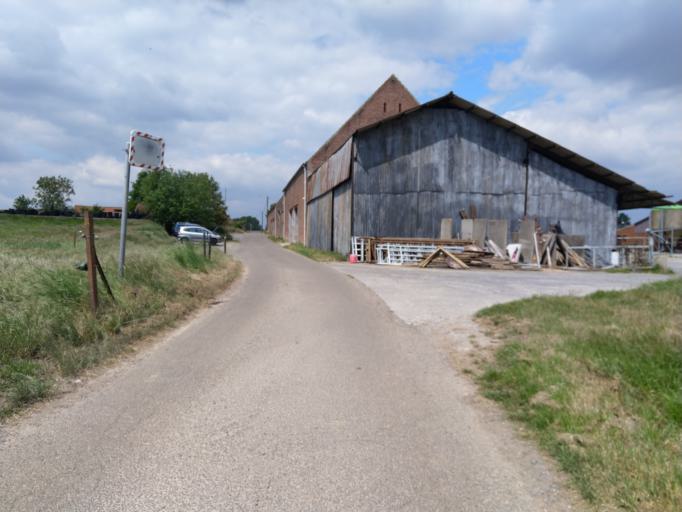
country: BE
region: Wallonia
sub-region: Province du Hainaut
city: Enghien
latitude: 50.6429
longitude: 4.0420
